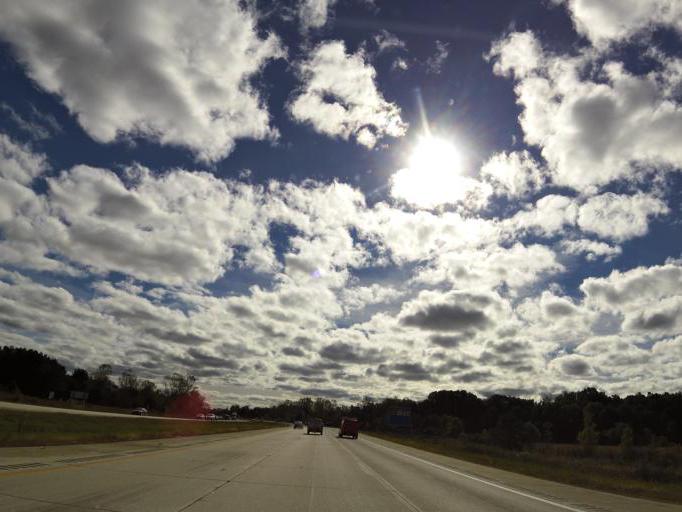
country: US
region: Michigan
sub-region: Genesee County
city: Burton
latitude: 43.0176
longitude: -83.5751
